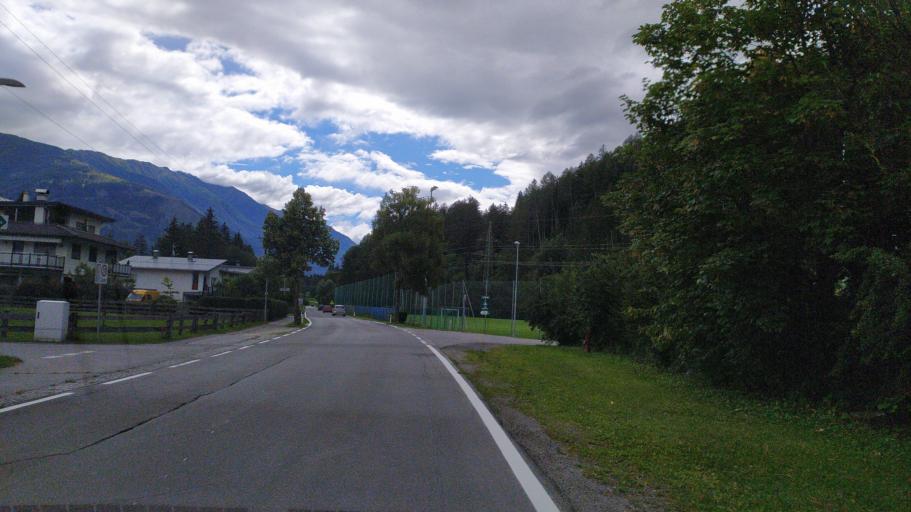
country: AT
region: Tyrol
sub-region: Politischer Bezirk Lienz
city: Tristach
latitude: 46.8151
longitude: 12.8005
